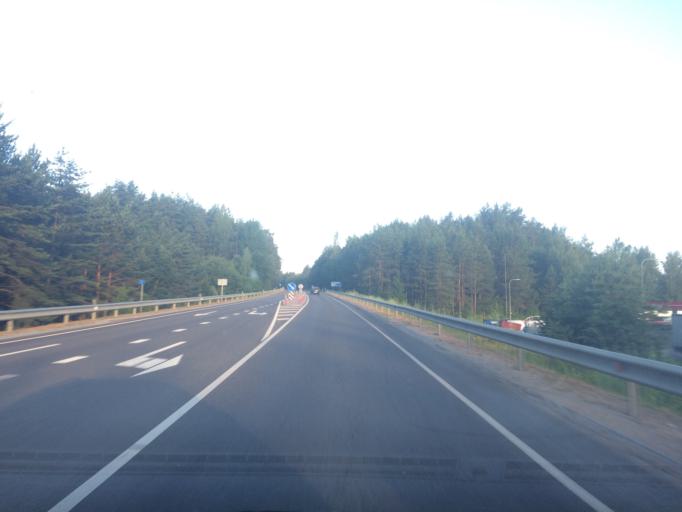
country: LT
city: Zarasai
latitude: 55.7175
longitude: 26.2152
